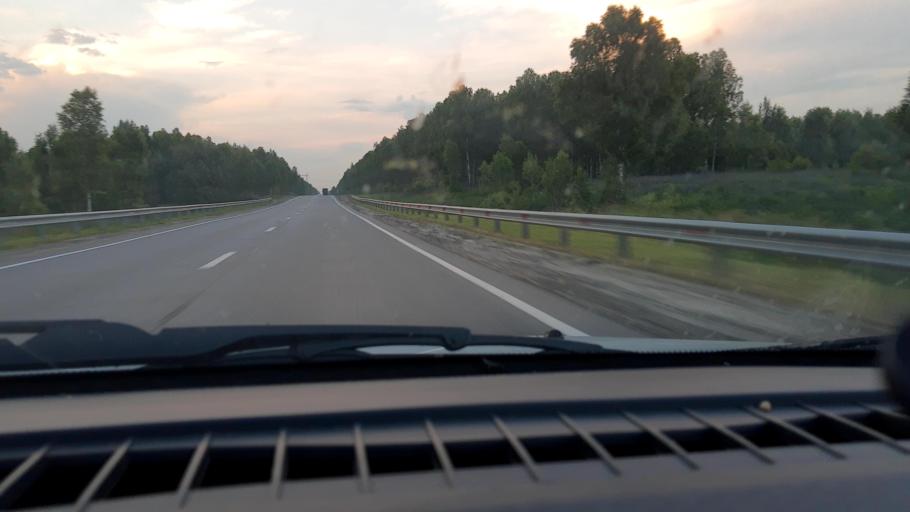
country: RU
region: Nizjnij Novgorod
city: Arzamas
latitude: 55.5506
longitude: 43.9423
